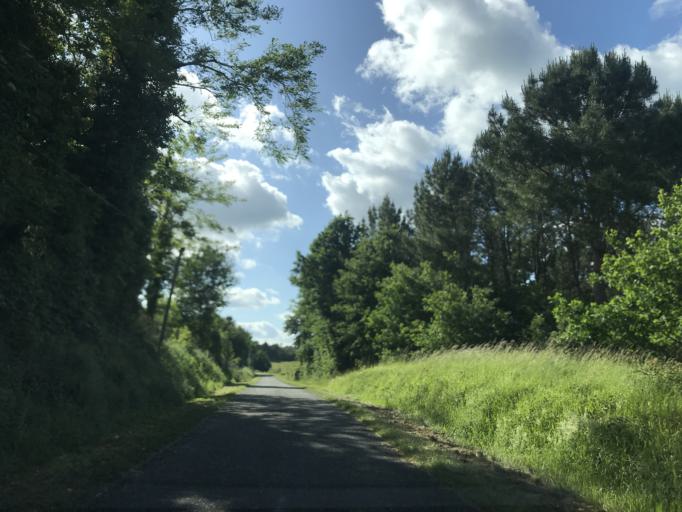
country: FR
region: Poitou-Charentes
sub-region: Departement de la Charente
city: Chalais
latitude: 45.2747
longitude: -0.0270
